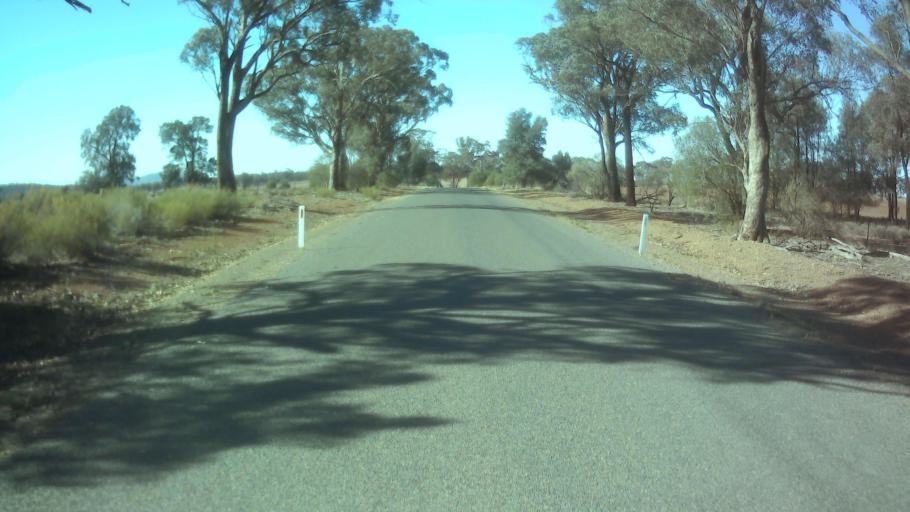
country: AU
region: New South Wales
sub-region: Forbes
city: Forbes
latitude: -33.6977
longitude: 147.8073
